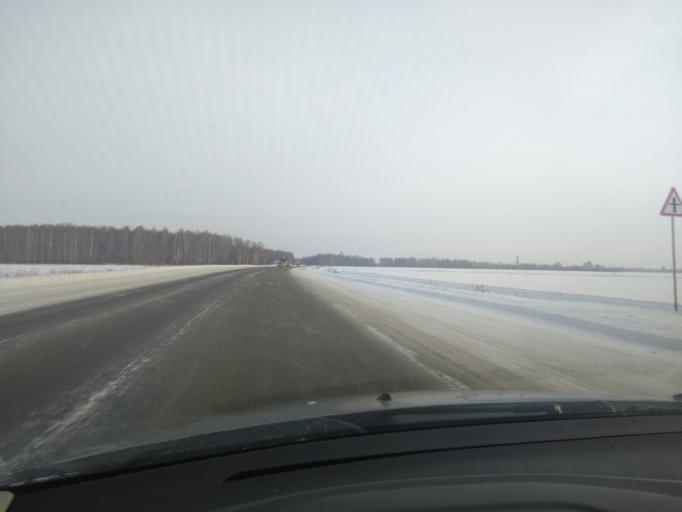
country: RU
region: Sverdlovsk
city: Bogdanovich
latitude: 56.7975
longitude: 62.0075
